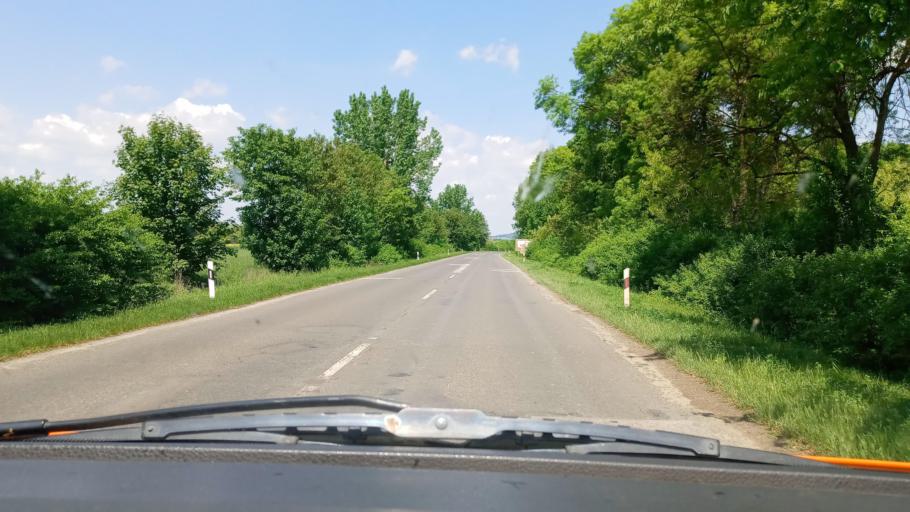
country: HU
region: Baranya
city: Harkany
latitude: 45.8177
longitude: 18.2159
